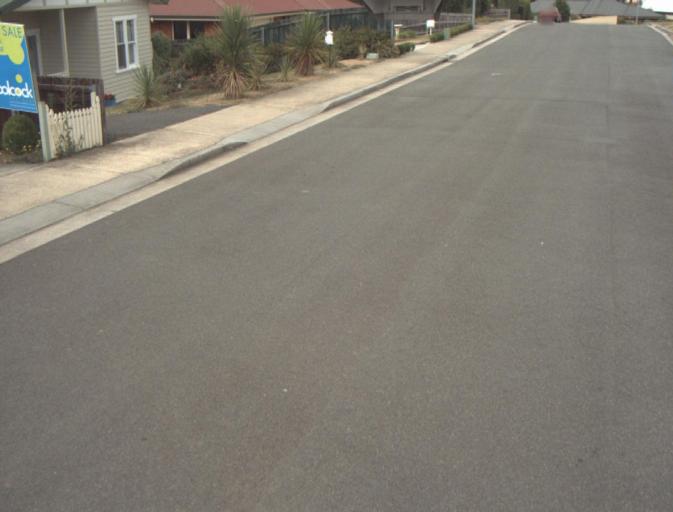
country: AU
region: Tasmania
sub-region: Launceston
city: Summerhill
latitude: -41.4835
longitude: 147.1736
